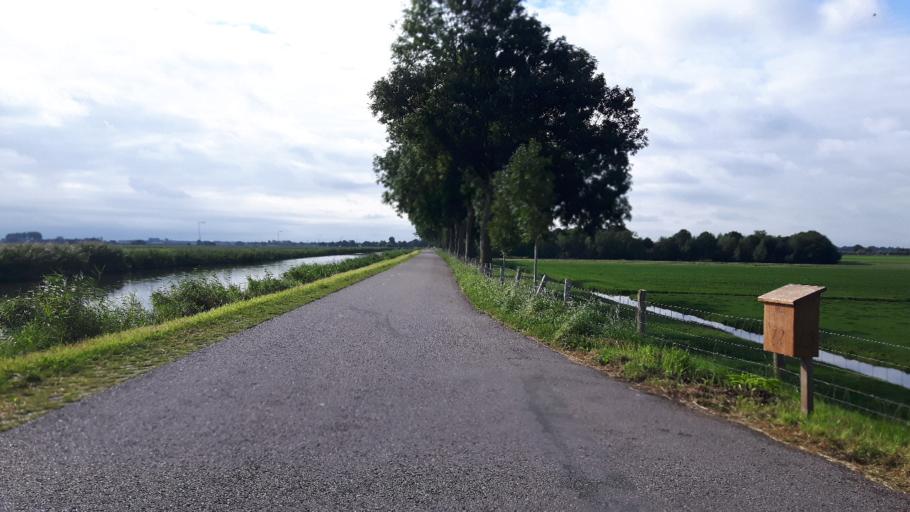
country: NL
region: North Holland
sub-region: Gemeente Purmerend
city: Purmerend
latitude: 52.5584
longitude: 4.9766
